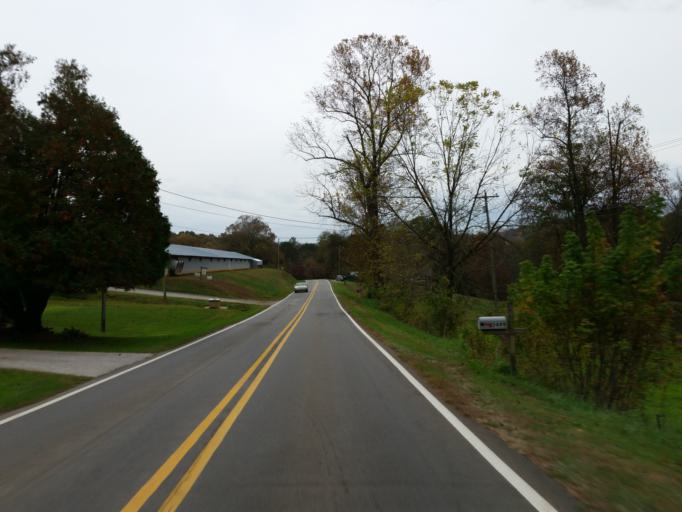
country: US
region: Georgia
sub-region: Gilmer County
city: Ellijay
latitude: 34.6489
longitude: -84.3487
